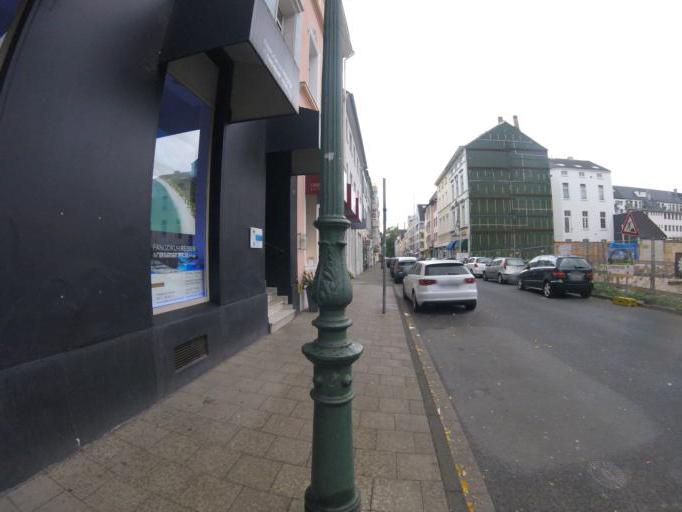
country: DE
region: North Rhine-Westphalia
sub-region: Regierungsbezirk Dusseldorf
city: Dusseldorf
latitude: 51.2216
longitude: 6.7753
